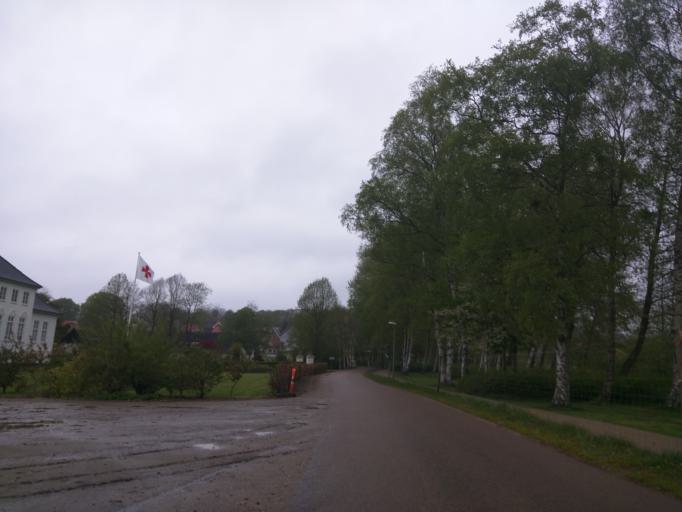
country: DK
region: Central Jutland
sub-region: Viborg Kommune
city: Viborg
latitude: 56.4381
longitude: 9.4052
